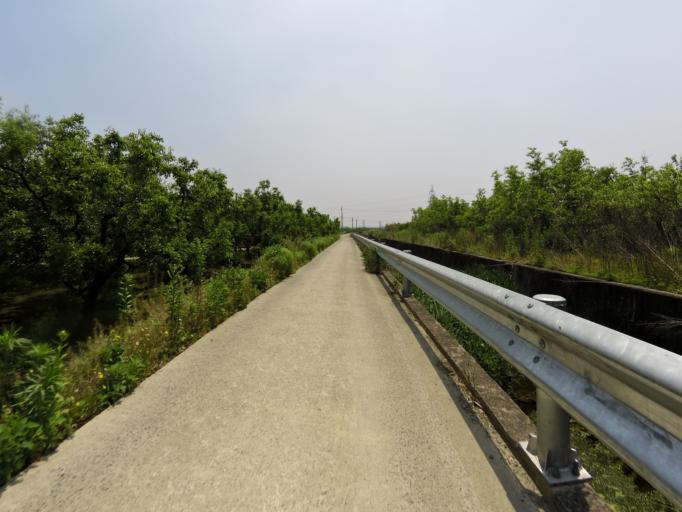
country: KR
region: Gyeongsangbuk-do
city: Gyeongsan-si
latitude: 35.8489
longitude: 128.7316
